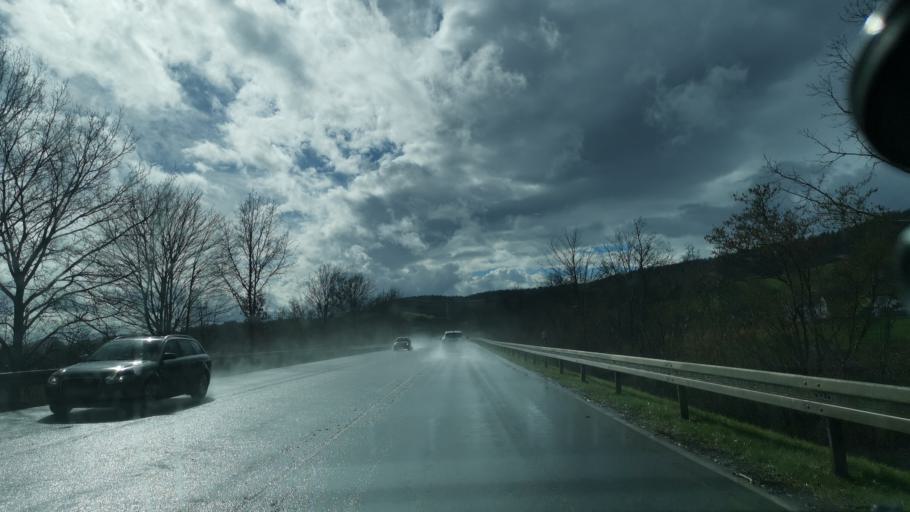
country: DE
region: Hesse
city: Breitenbach
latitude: 50.9467
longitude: 9.7766
